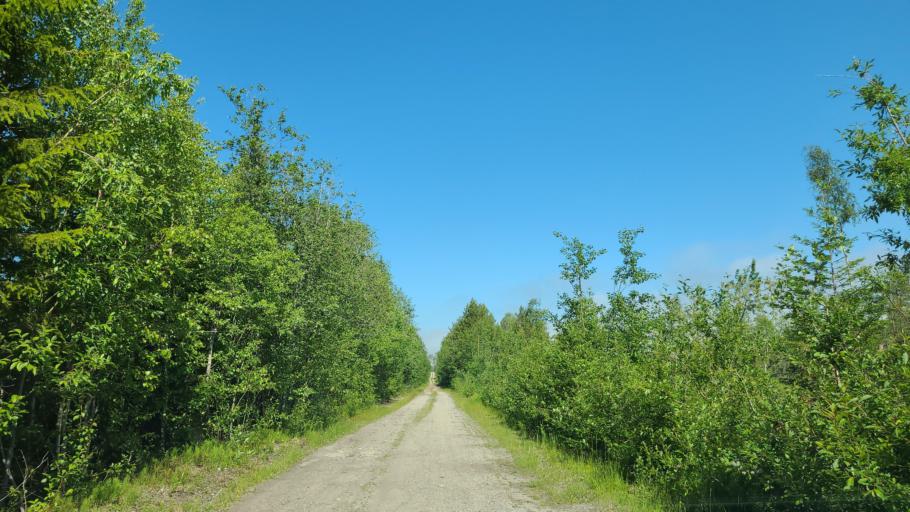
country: SE
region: Vaesternorrland
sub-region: OErnskoeldsviks Kommun
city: Husum
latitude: 63.4272
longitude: 19.2267
